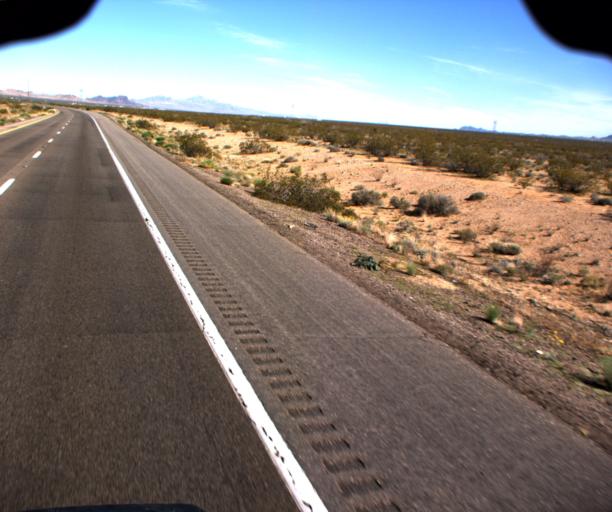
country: US
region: Arizona
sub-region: Mohave County
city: Dolan Springs
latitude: 35.6591
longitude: -114.4478
